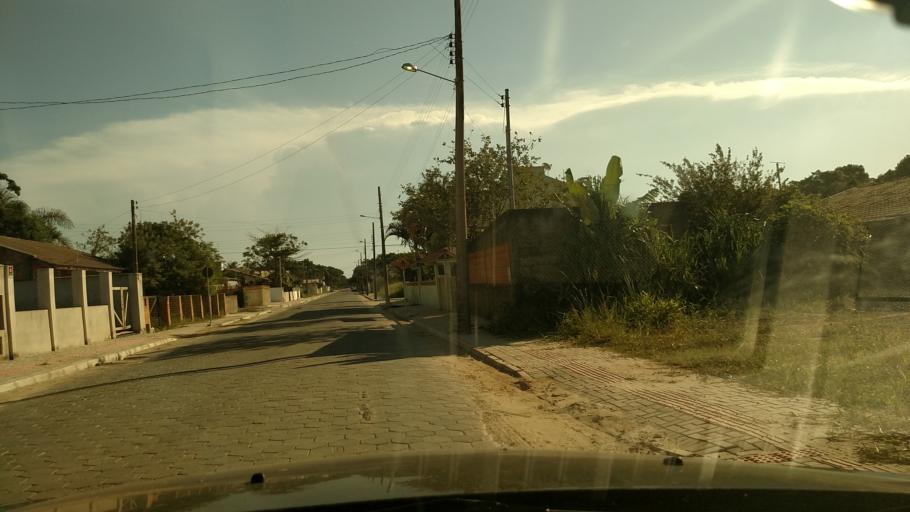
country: BR
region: Santa Catarina
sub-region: Porto Belo
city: Porto Belo
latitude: -27.1779
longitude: -48.5070
